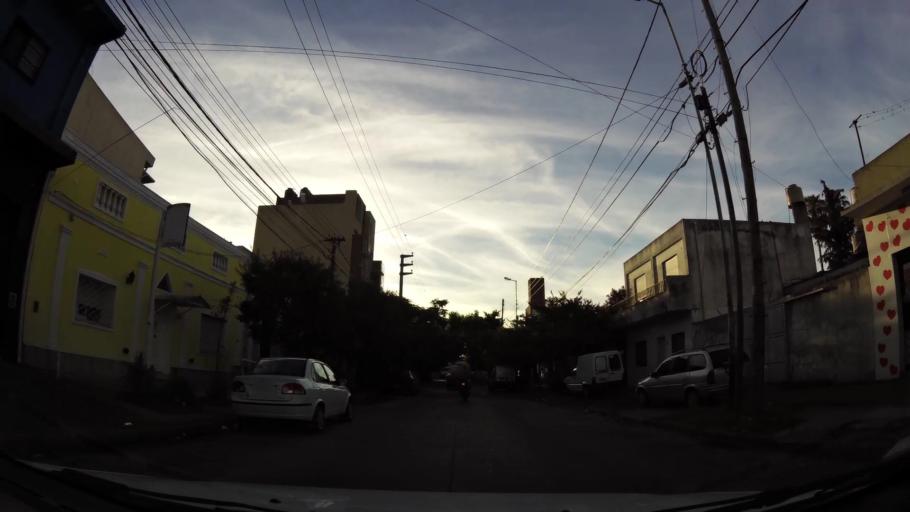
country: AR
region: Buenos Aires
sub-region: Partido de Moron
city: Moron
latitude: -34.6454
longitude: -58.6243
